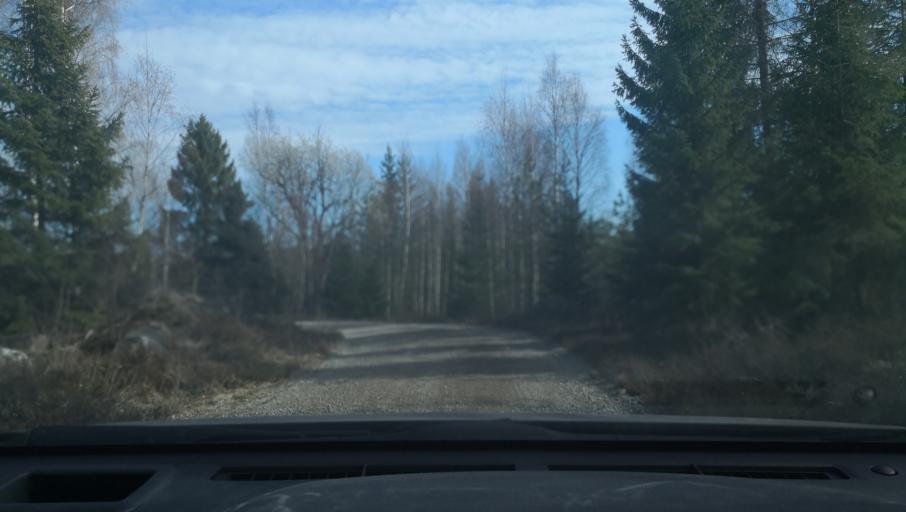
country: SE
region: Uppsala
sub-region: Heby Kommun
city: Heby
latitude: 59.8400
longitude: 16.8646
